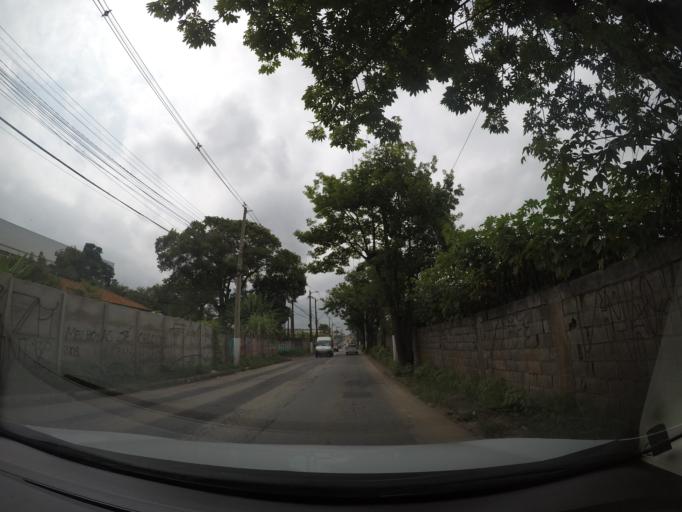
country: BR
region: Sao Paulo
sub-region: Itaquaquecetuba
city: Itaquaquecetuba
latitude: -23.4383
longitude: -46.3962
